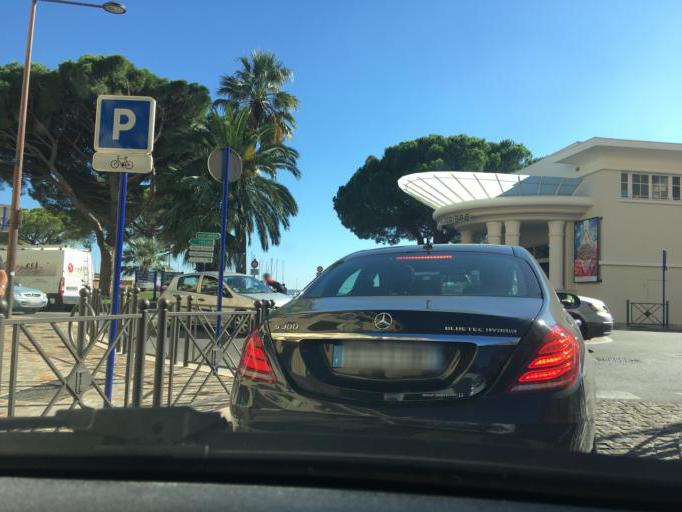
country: FR
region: Provence-Alpes-Cote d'Azur
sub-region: Departement du Var
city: Sainte-Maxime
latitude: 43.3086
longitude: 6.6365
